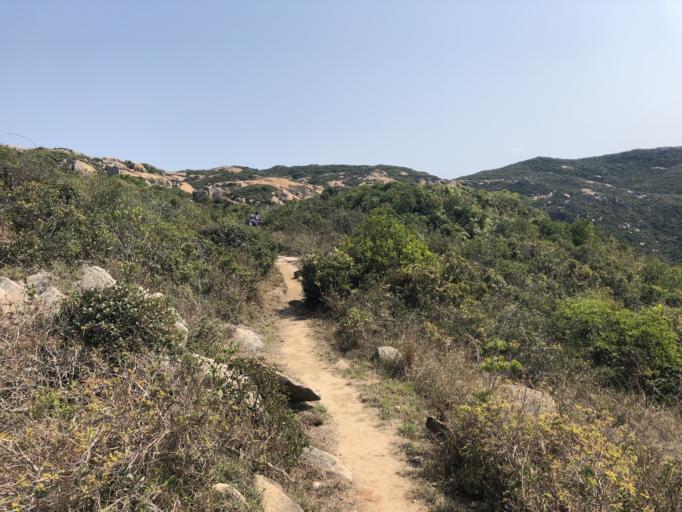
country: HK
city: Sok Kwu Wan
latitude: 22.1681
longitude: 114.2535
